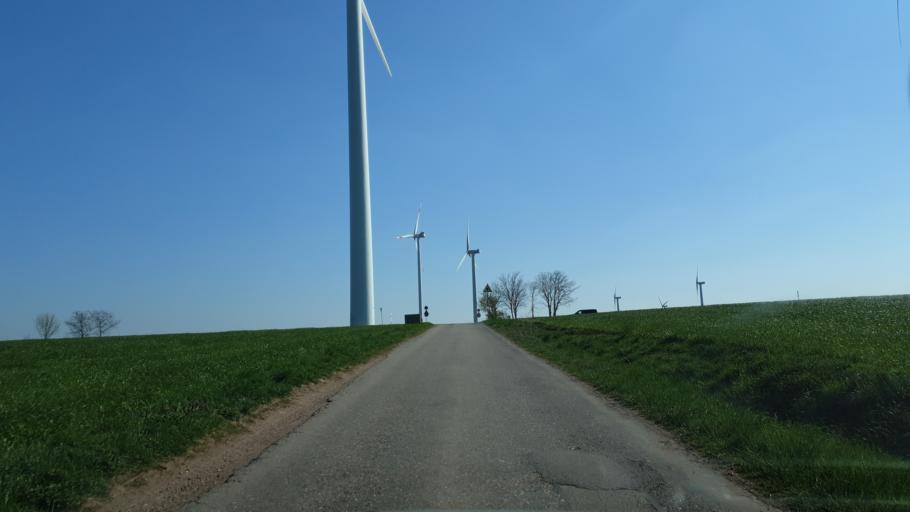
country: DE
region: Saxony
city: Hohndorf
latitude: 50.7660
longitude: 12.6843
